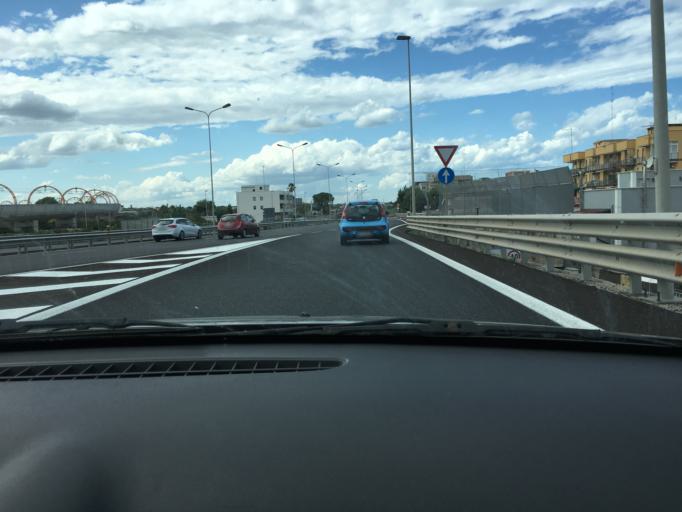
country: IT
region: Apulia
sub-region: Provincia di Bari
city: San Paolo
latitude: 41.1357
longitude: 16.8131
